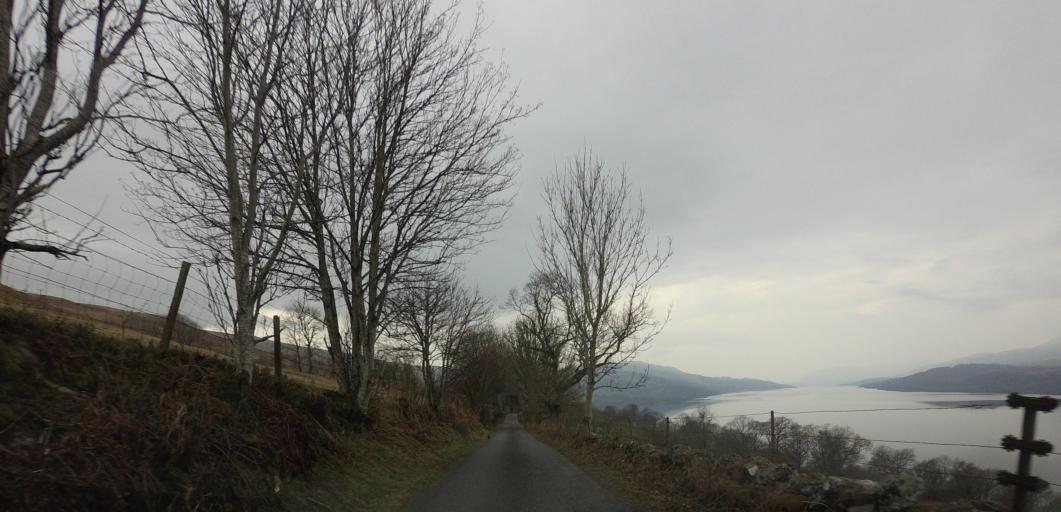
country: GB
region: Scotland
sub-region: Perth and Kinross
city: Comrie
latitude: 56.5137
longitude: -4.1323
